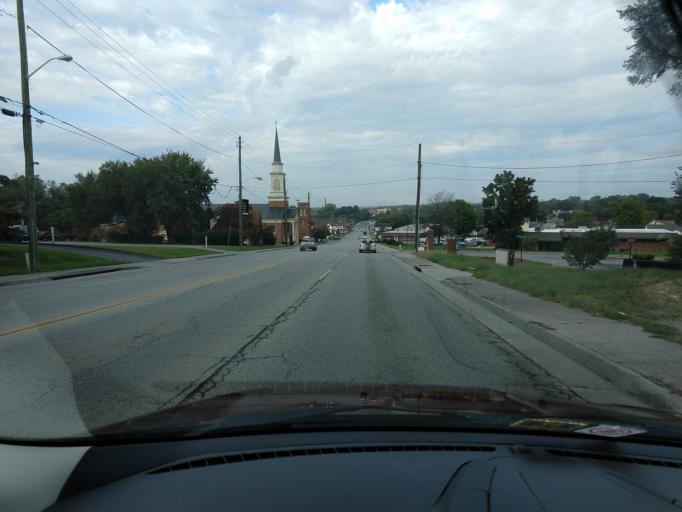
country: US
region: Virginia
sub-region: Roanoke County
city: Vinton
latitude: 37.2806
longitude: -79.8934
